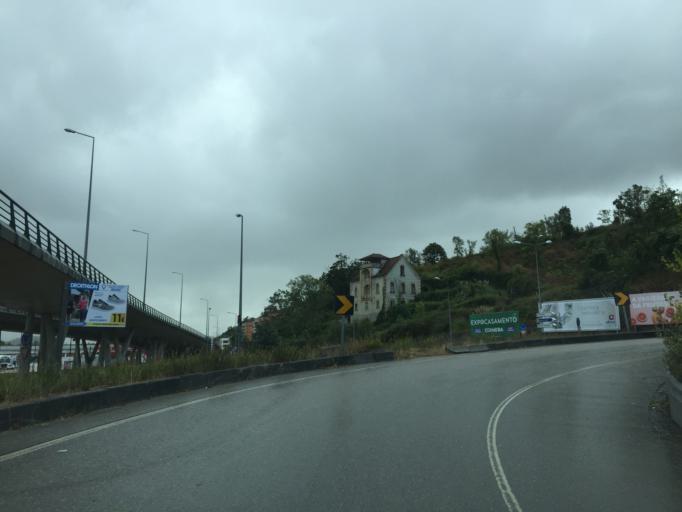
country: PT
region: Coimbra
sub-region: Coimbra
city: Coimbra
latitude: 40.2121
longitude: -8.4408
